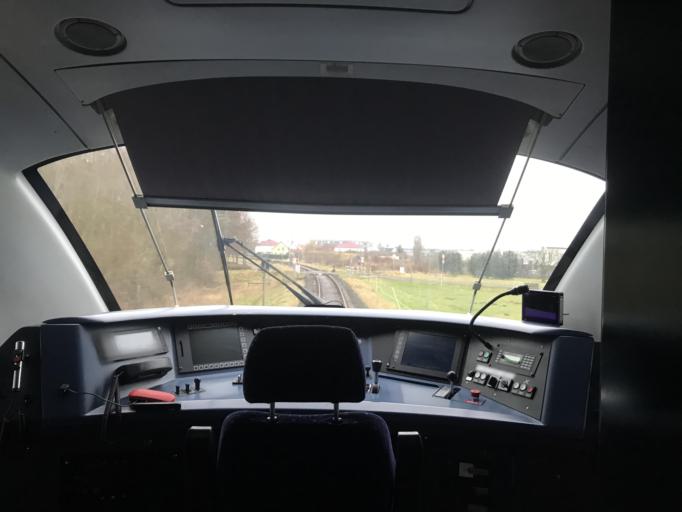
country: DE
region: Hesse
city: Fritzlar
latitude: 51.1227
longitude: 9.2704
